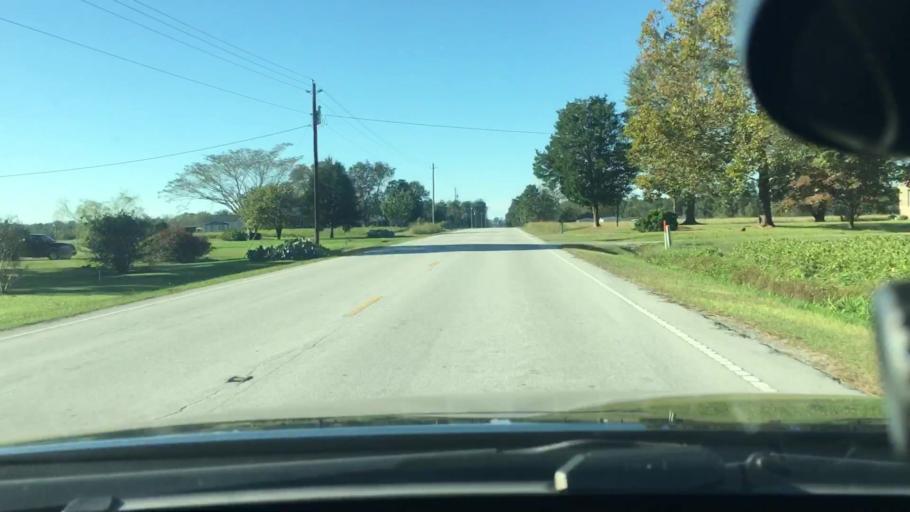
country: US
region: North Carolina
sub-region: Craven County
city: Vanceboro
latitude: 35.3625
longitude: -77.1991
